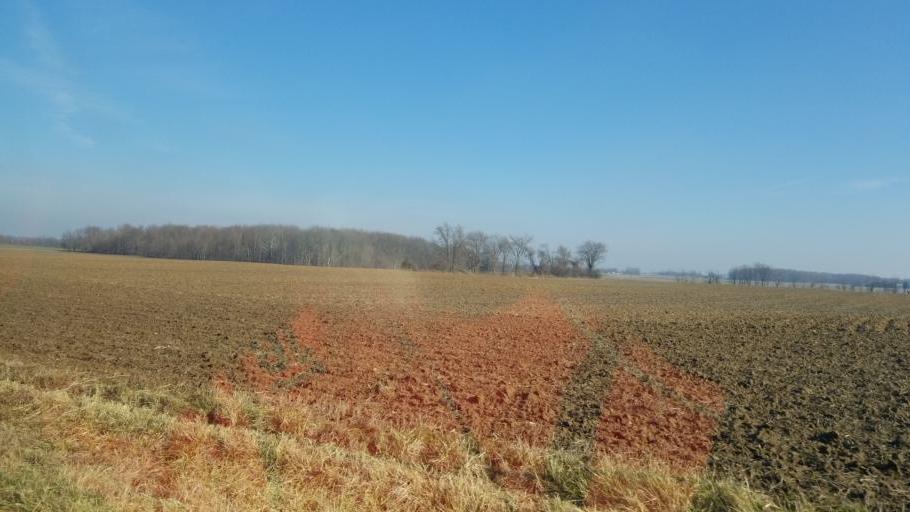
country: US
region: Ohio
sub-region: Seneca County
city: Tiffin
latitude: 41.0253
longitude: -83.0741
